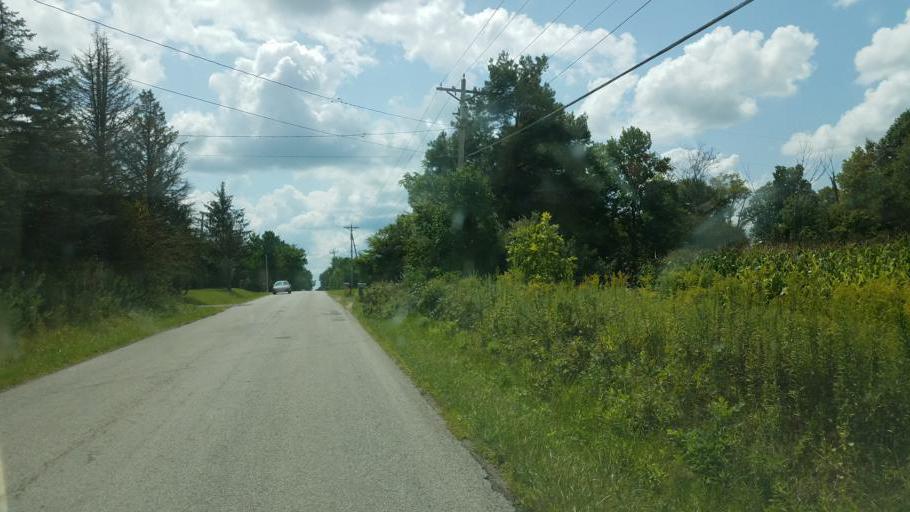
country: US
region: Ohio
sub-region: Morrow County
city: Mount Gilead
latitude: 40.4378
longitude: -82.7854
